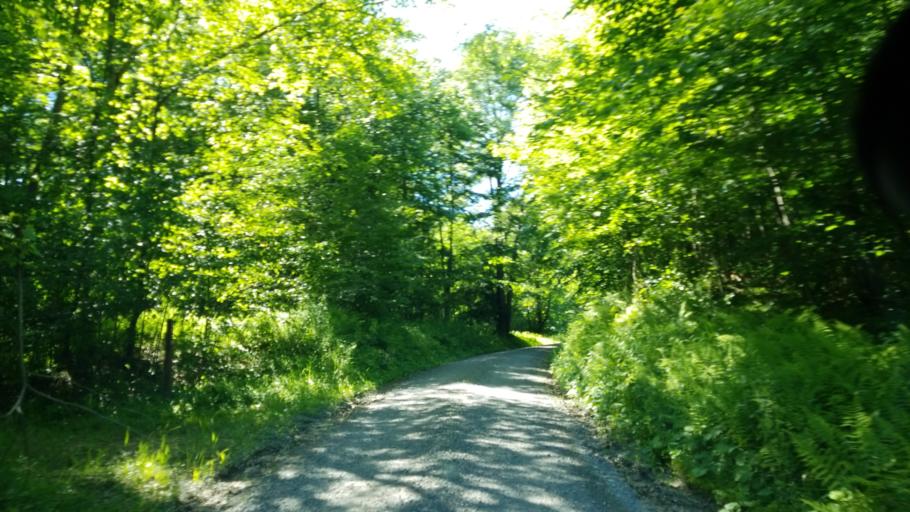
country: US
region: Pennsylvania
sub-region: Clearfield County
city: Clearfield
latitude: 41.2099
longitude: -78.3886
